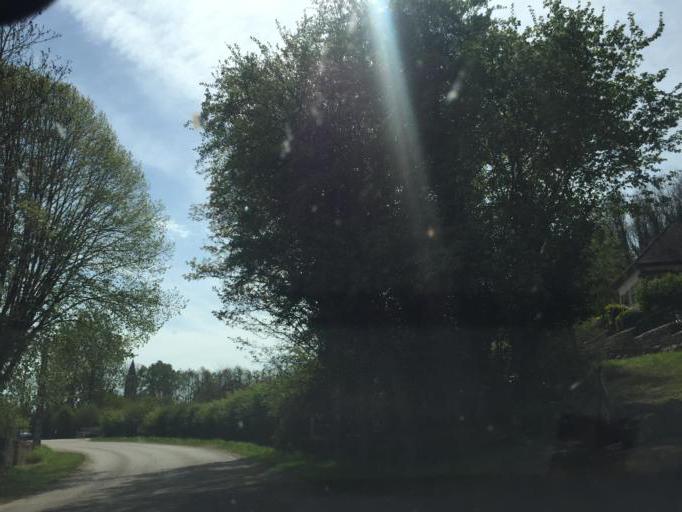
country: FR
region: Bourgogne
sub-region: Departement de l'Yonne
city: Avallon
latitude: 47.4610
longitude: 3.7613
